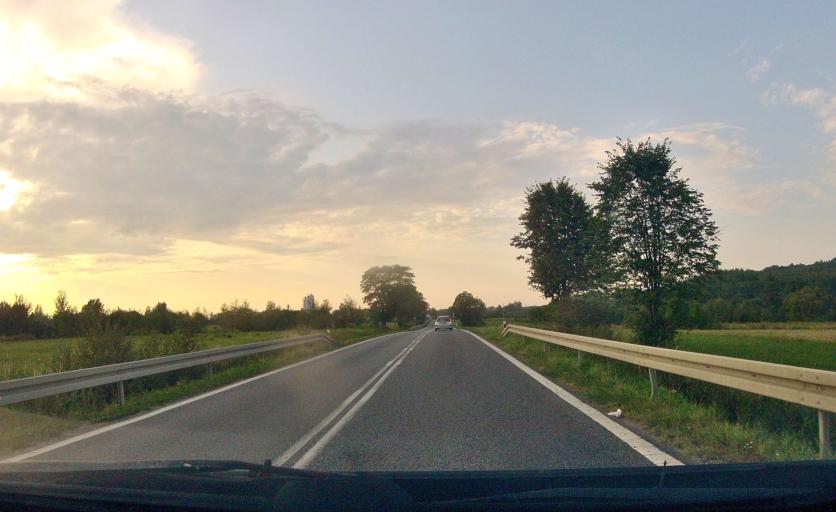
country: PL
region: Subcarpathian Voivodeship
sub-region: Powiat jasielski
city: Osiek Jasielski
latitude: 49.6504
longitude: 21.5076
